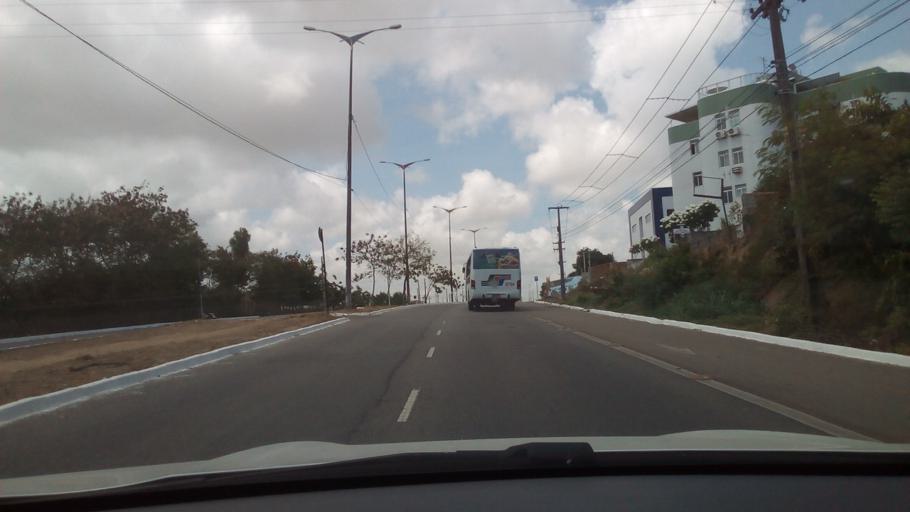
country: BR
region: Paraiba
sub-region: Joao Pessoa
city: Joao Pessoa
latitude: -7.1604
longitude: -34.8162
